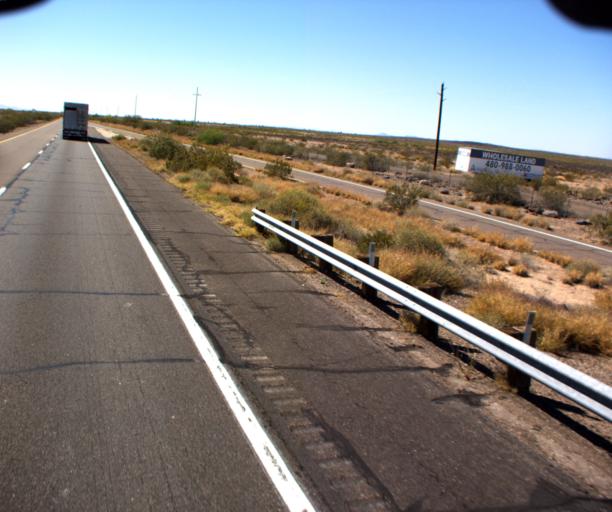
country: US
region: Arizona
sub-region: Maricopa County
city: Gila Bend
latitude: 32.8583
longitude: -113.2161
